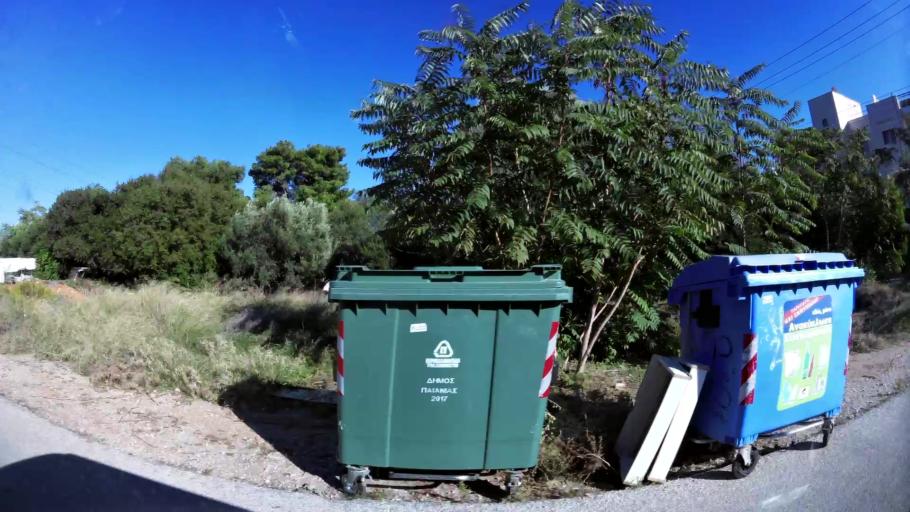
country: GR
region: Attica
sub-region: Nomarchia Anatolikis Attikis
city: Leondarion
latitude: 37.9928
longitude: 23.8445
